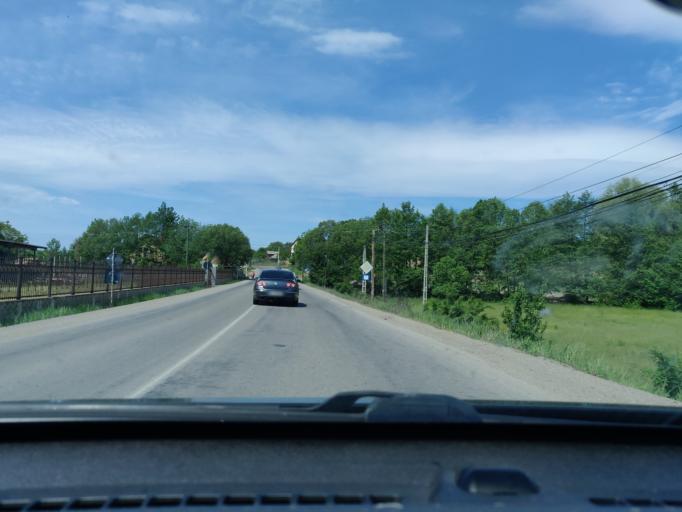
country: RO
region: Vrancea
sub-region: Comuna Vidra
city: Vidra
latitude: 45.9108
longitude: 26.9224
